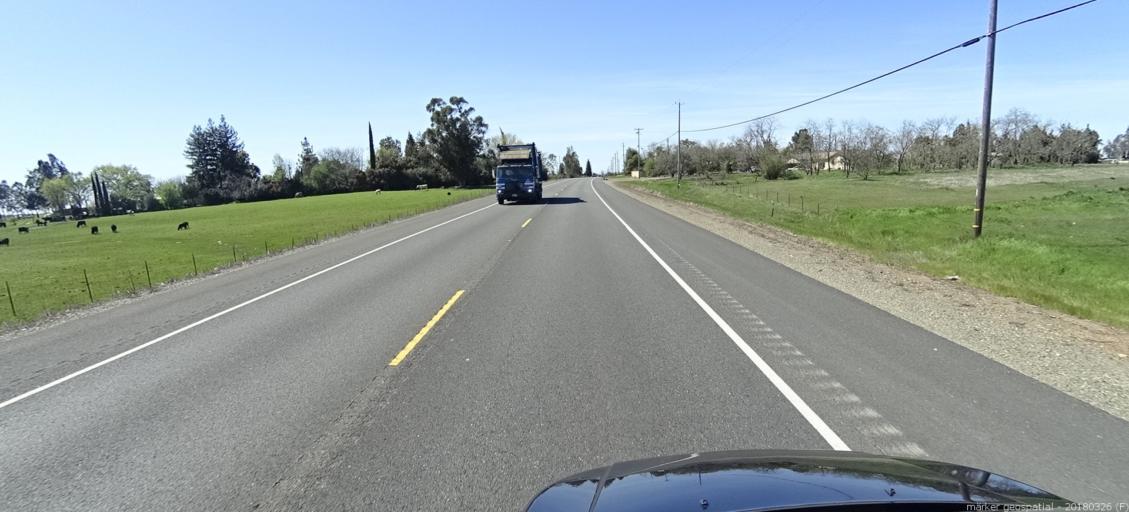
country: US
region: California
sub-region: Sacramento County
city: Rancho Cordova
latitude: 38.5126
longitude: -121.2741
